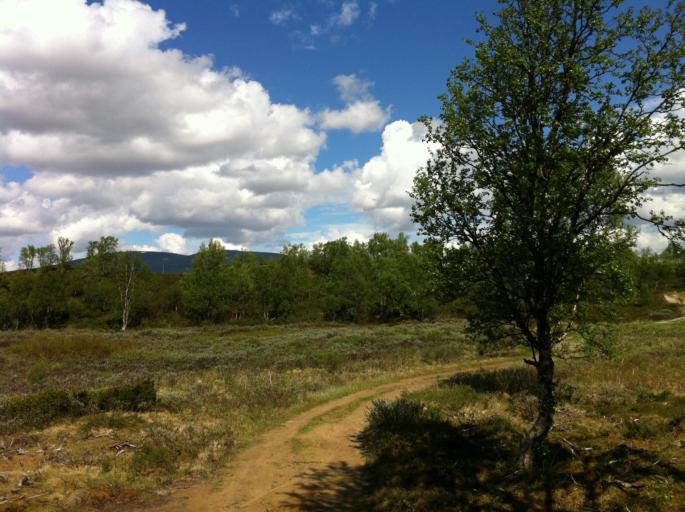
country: SE
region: Jaemtland
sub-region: Are Kommun
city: Are
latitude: 62.7089
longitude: 12.4973
